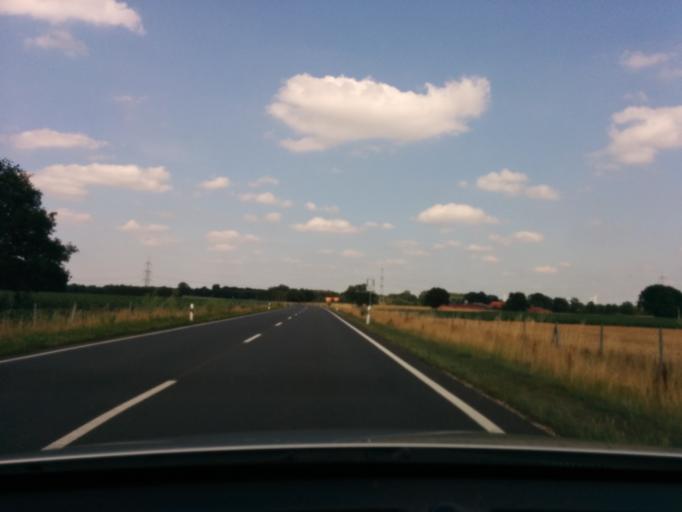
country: DE
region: North Rhine-Westphalia
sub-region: Regierungsbezirk Munster
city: Wettringen
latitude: 52.2063
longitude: 7.3541
